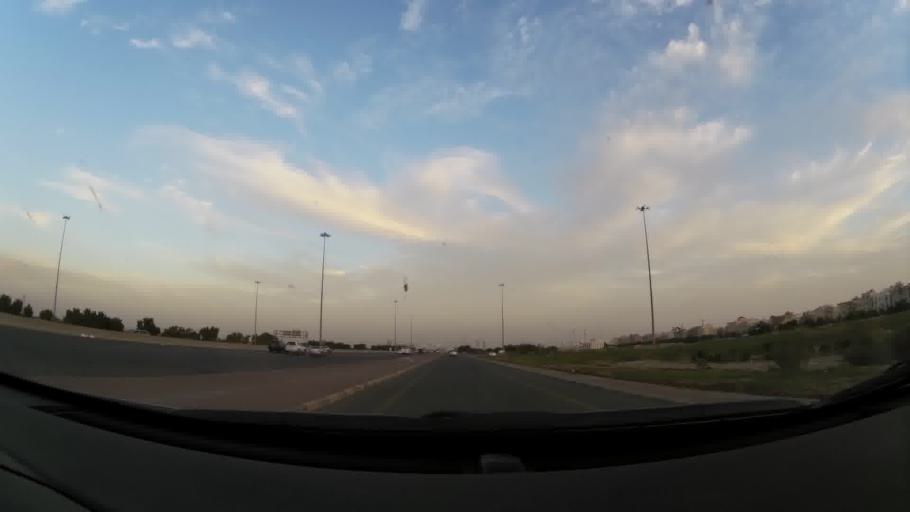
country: KW
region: Muhafazat al Jahra'
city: Al Jahra'
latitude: 29.3113
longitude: 47.7879
